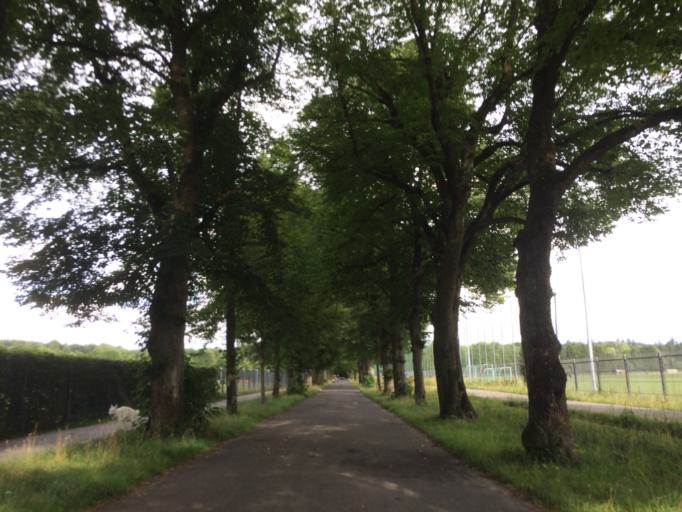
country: DE
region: Bavaria
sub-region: Swabia
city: Augsburg
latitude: 48.3393
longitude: 10.9104
